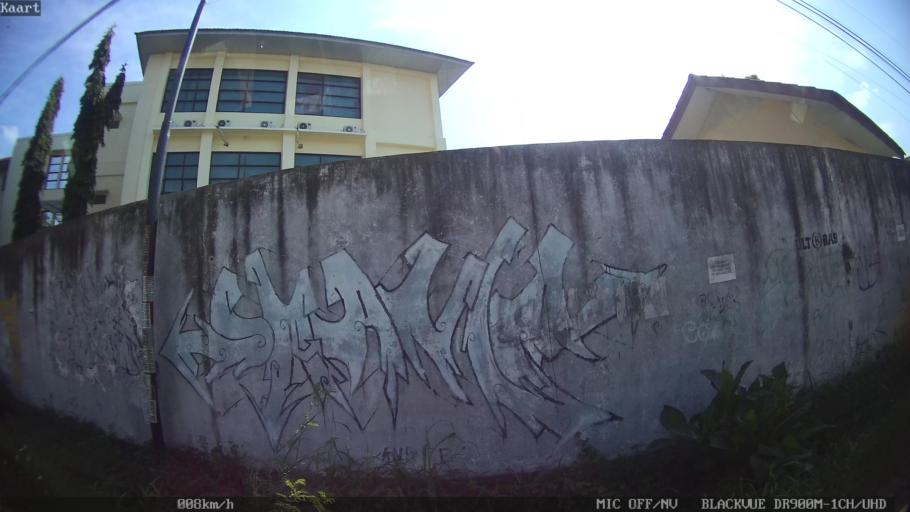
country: ID
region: Lampung
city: Kedaton
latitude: -5.3681
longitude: 105.2480
